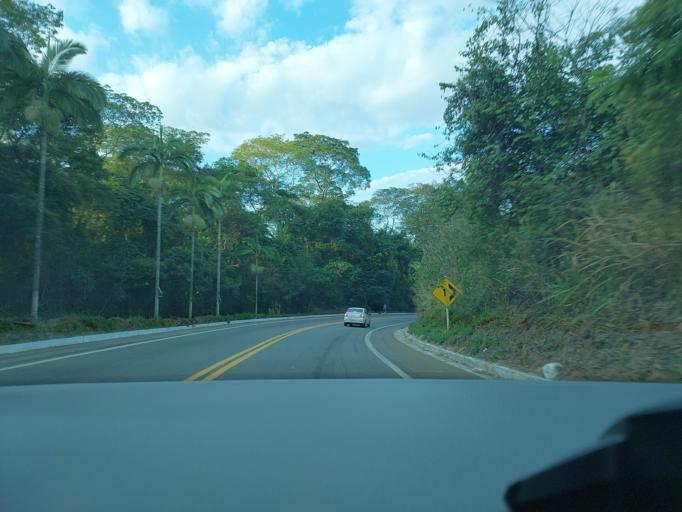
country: BR
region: Minas Gerais
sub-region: Muriae
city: Muriae
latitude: -21.1246
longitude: -42.2819
